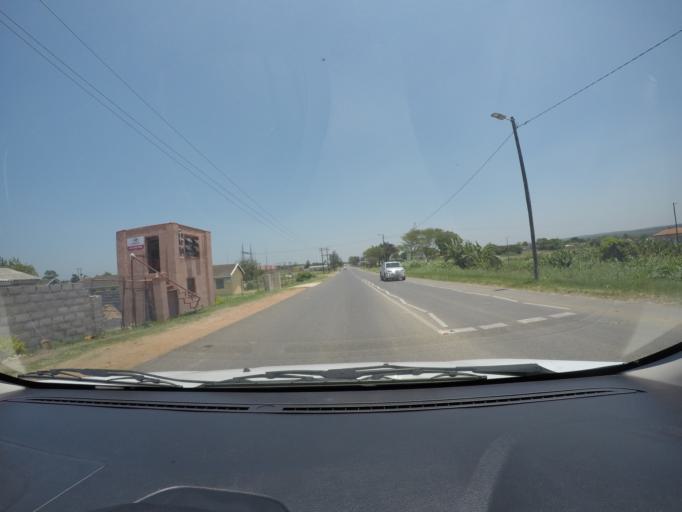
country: ZA
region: KwaZulu-Natal
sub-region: uThungulu District Municipality
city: eSikhawini
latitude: -28.8846
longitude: 31.9016
